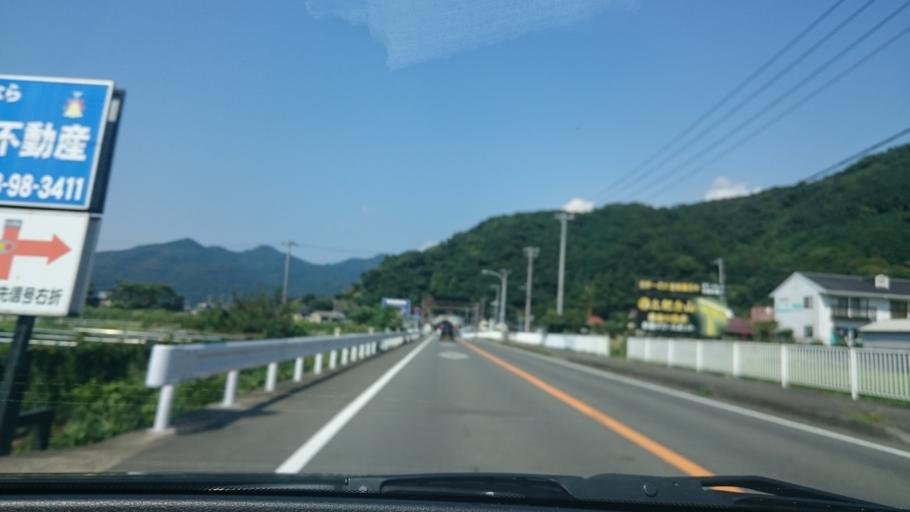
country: JP
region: Shizuoka
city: Heda
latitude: 34.8930
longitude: 138.7754
